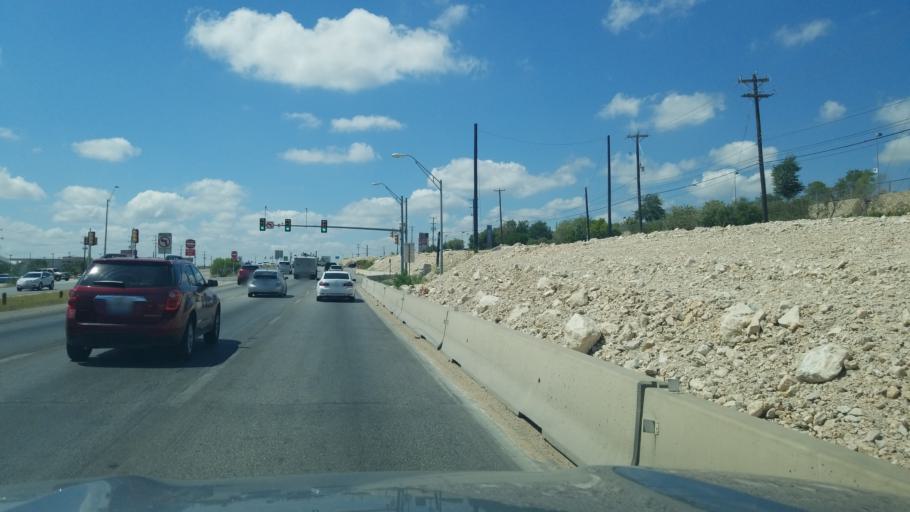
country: US
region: Texas
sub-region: Bexar County
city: Hollywood Park
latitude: 29.6407
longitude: -98.4541
